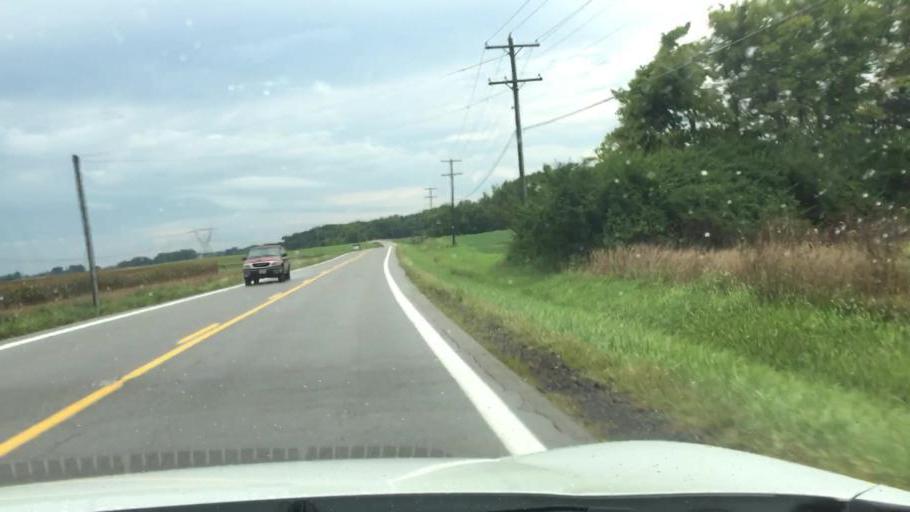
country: US
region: Ohio
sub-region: Madison County
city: West Jefferson
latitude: 39.9707
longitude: -83.3712
